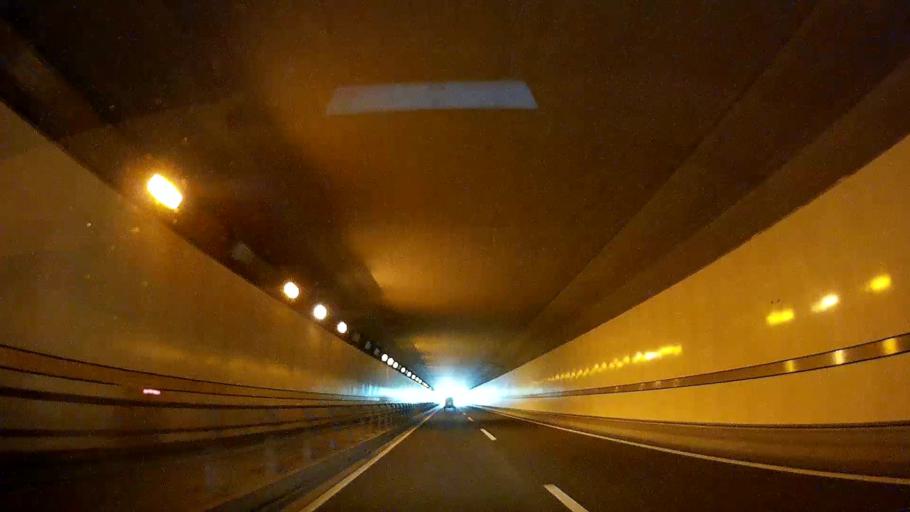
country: JP
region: Kanagawa
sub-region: Kawasaki-shi
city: Kawasaki
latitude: 35.5452
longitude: 139.7906
